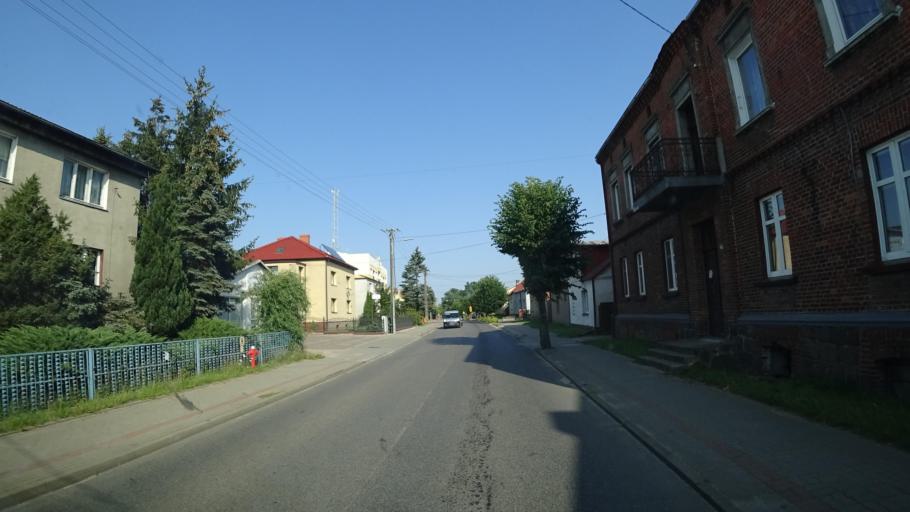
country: PL
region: Pomeranian Voivodeship
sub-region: Powiat czluchowski
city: Przechlewo
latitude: 53.8000
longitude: 17.2570
